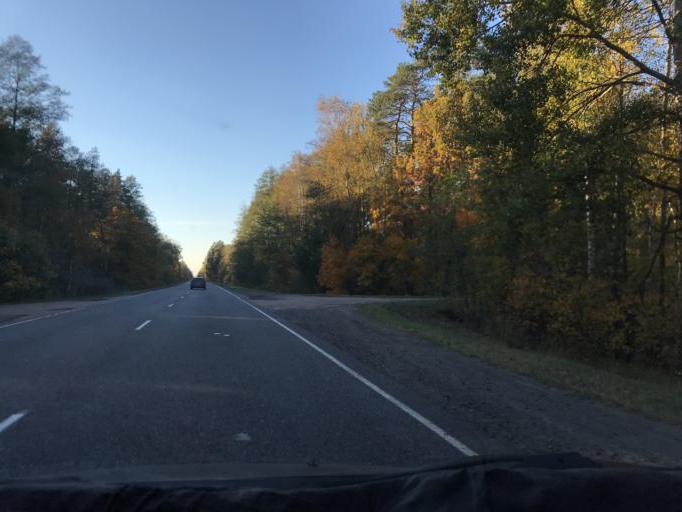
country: BY
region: Gomel
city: Pyetrykaw
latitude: 52.2575
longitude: 28.3429
